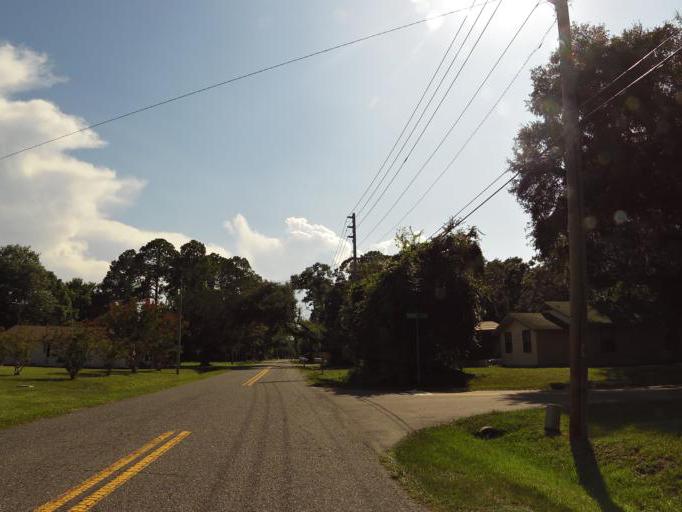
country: US
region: Florida
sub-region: Nassau County
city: Fernandina Beach
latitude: 30.6383
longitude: -81.4604
